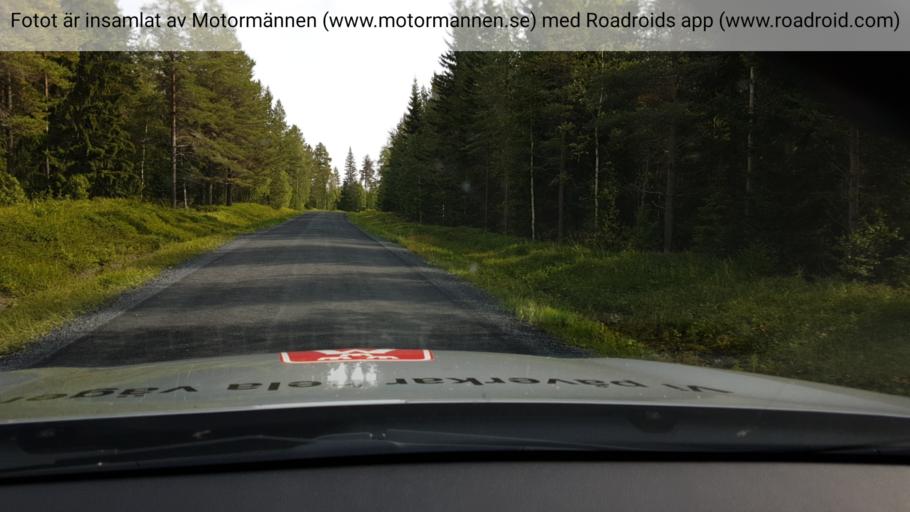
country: SE
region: Jaemtland
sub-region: Krokoms Kommun
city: Valla
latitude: 63.3667
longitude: 13.8897
